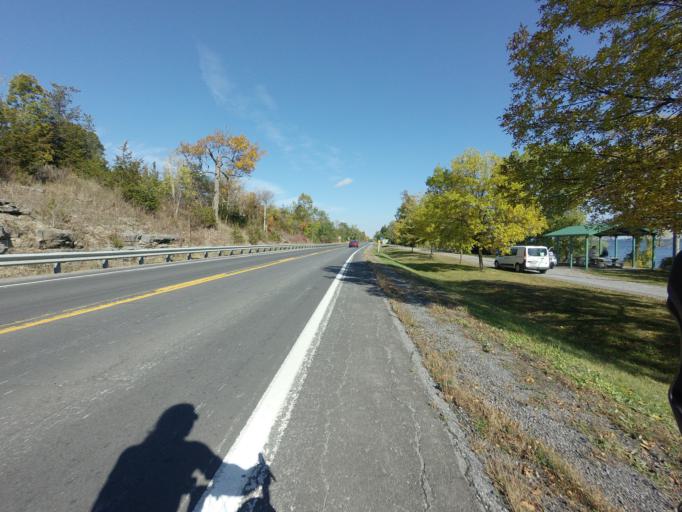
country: CA
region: Ontario
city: Skatepark
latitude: 44.1863
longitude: -76.7521
